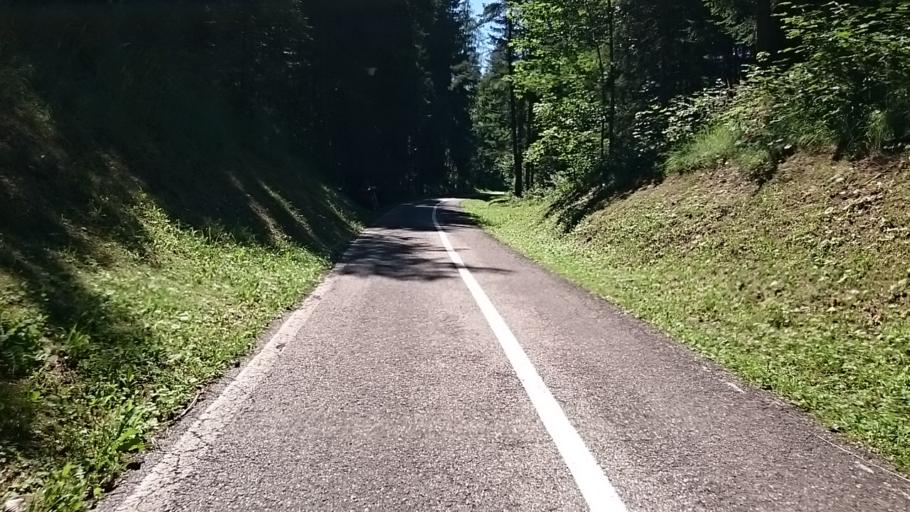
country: IT
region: Veneto
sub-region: Provincia di Belluno
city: San Vito
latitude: 46.4704
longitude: 12.2063
